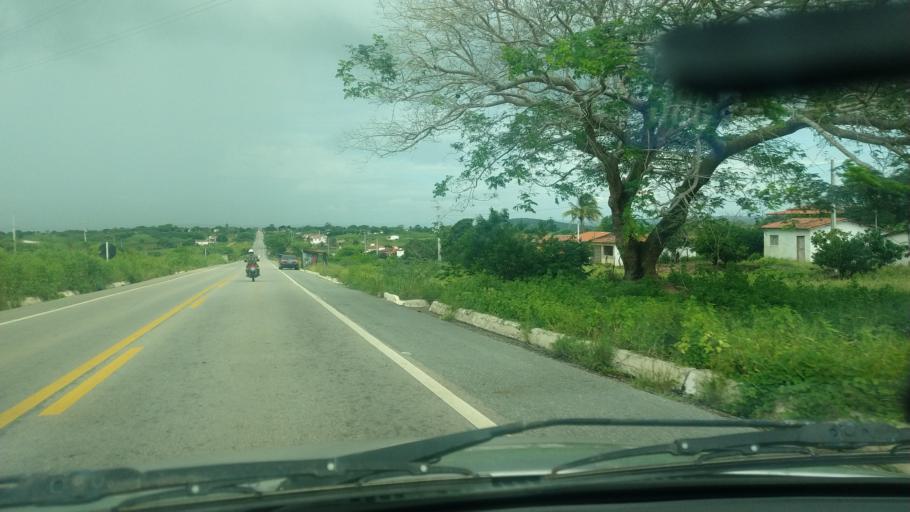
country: BR
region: Rio Grande do Norte
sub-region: Santa Cruz
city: Santa Cruz
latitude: -6.1954
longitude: -36.2050
